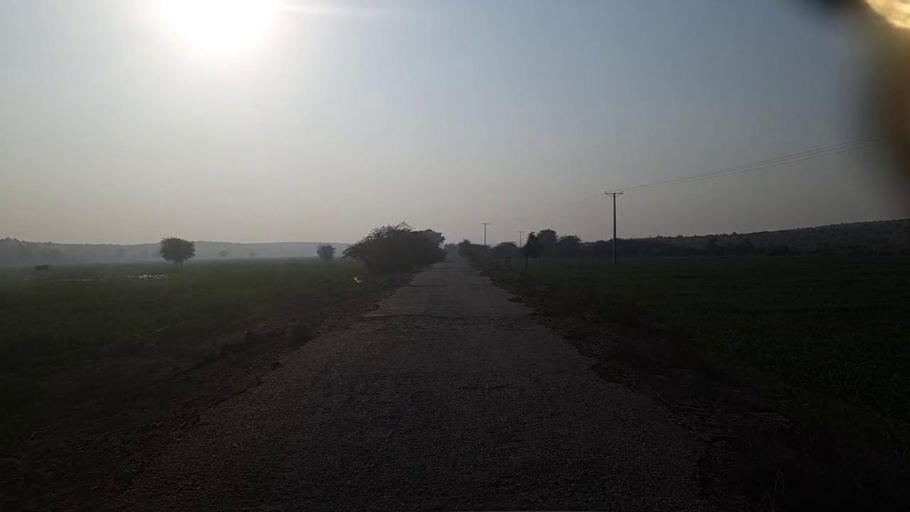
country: PK
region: Sindh
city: Pad Idan
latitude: 26.7152
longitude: 68.4833
